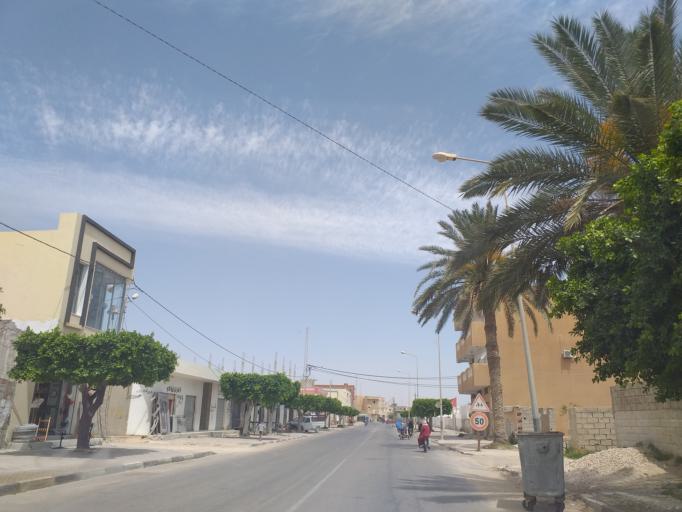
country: TN
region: Qabis
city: Gabes
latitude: 33.9341
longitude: 10.0705
